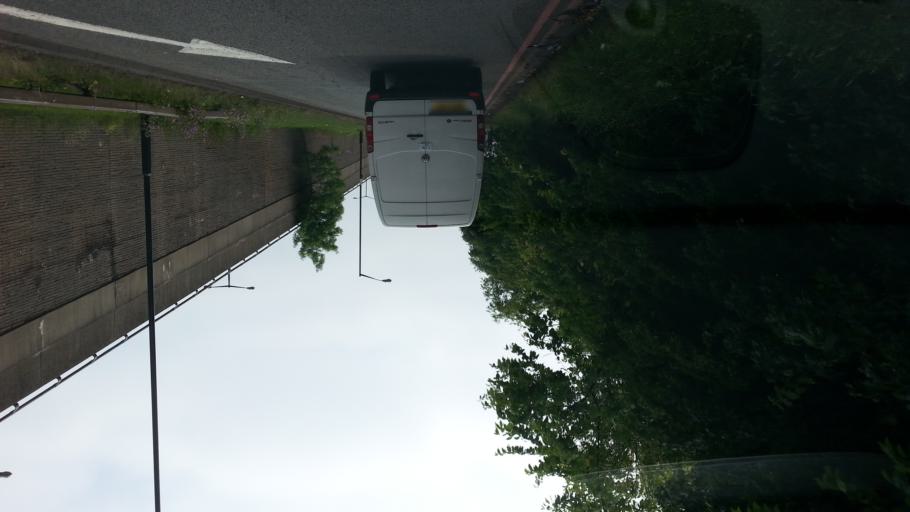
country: GB
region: England
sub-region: City and Borough of Birmingham
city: Hockley
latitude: 52.5523
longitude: -1.9342
